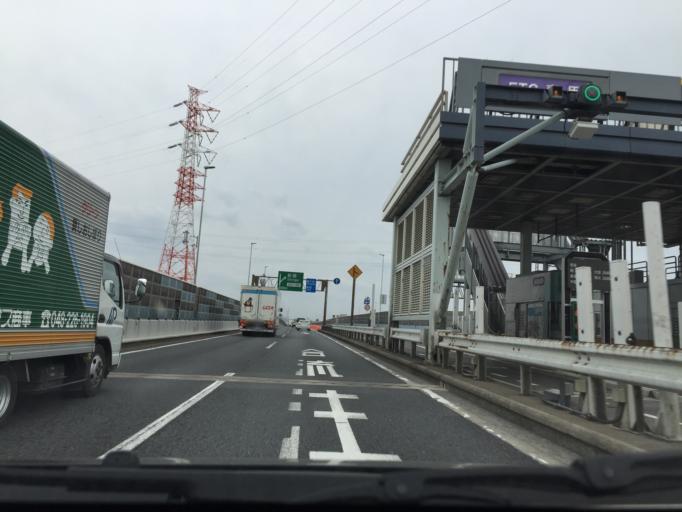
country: JP
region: Saitama
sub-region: Kawaguchi-shi
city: Hatogaya-honcho
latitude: 35.8320
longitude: 139.7568
